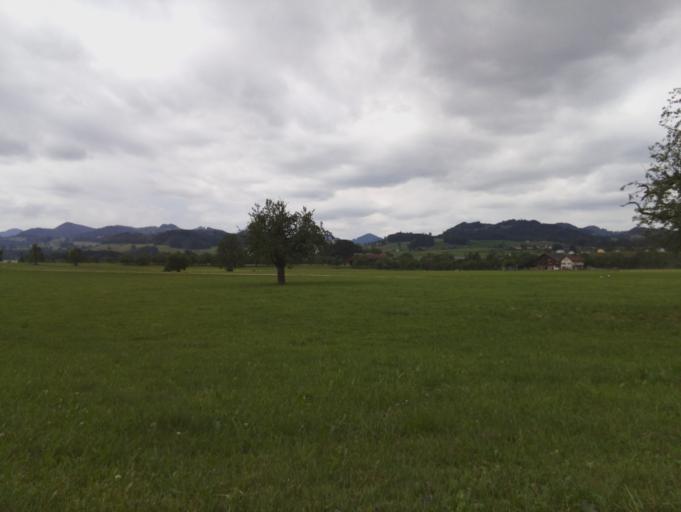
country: CH
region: Saint Gallen
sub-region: Wahlkreis Toggenburg
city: Lutisburg
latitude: 47.3890
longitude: 9.0873
